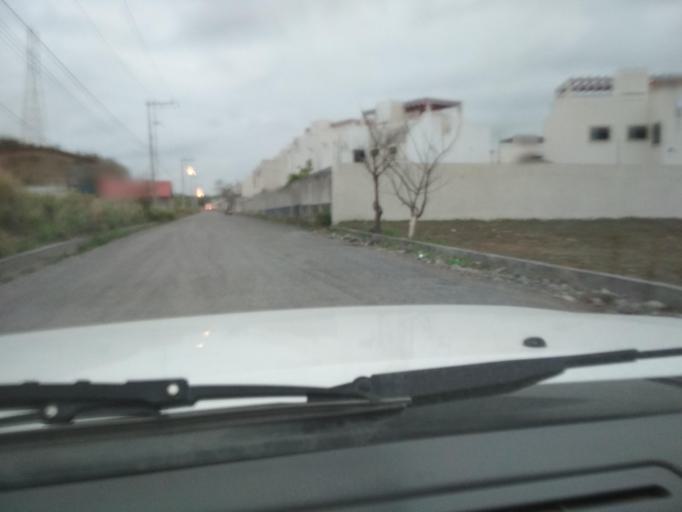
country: MX
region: Veracruz
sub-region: Medellin
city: Fraccionamiento Arboledas San Ramon
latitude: 19.0900
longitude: -96.1294
